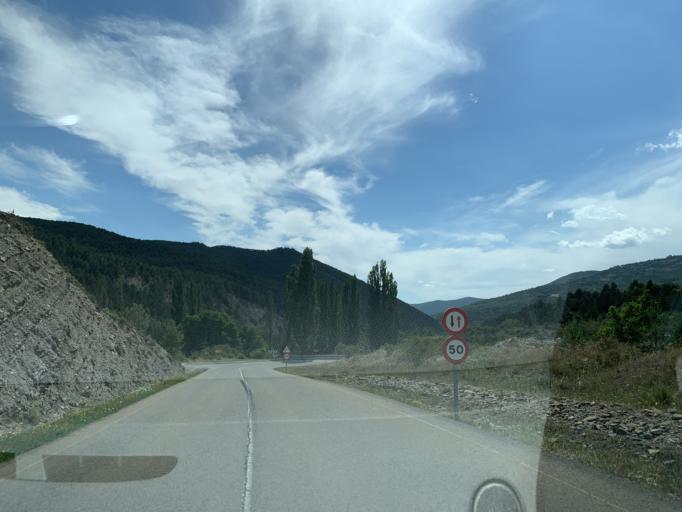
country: ES
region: Aragon
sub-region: Provincia de Huesca
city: Borau
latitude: 42.6568
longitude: -0.6317
